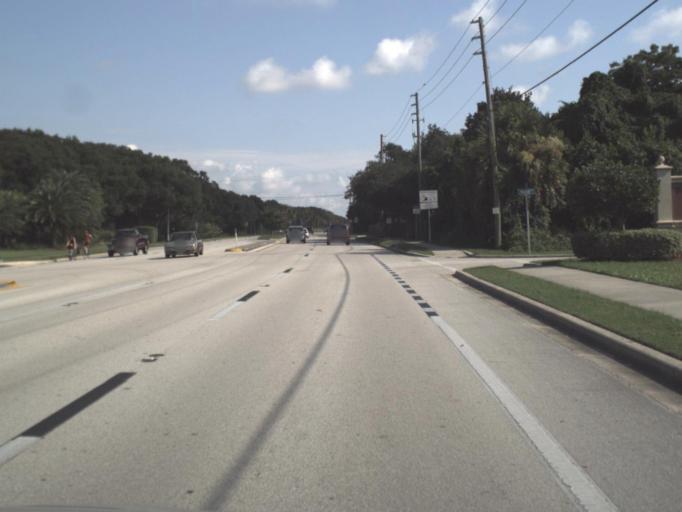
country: US
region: Florida
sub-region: Saint Johns County
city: Saint Augustine Beach
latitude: 29.8312
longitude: -81.2733
